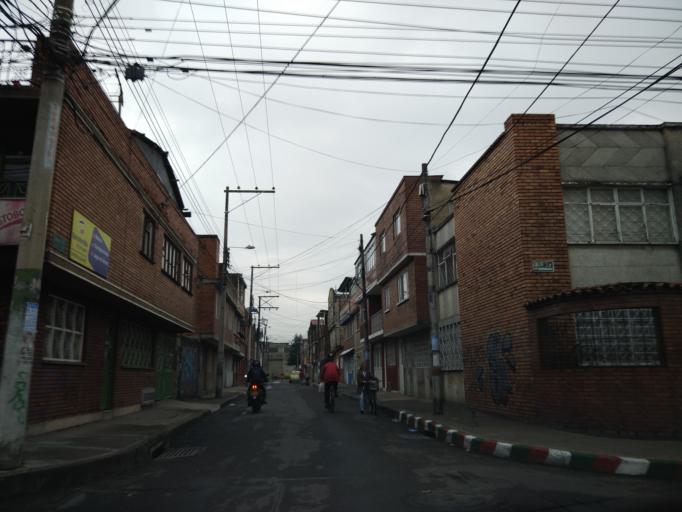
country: CO
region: Cundinamarca
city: Funza
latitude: 4.6784
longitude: -74.1445
